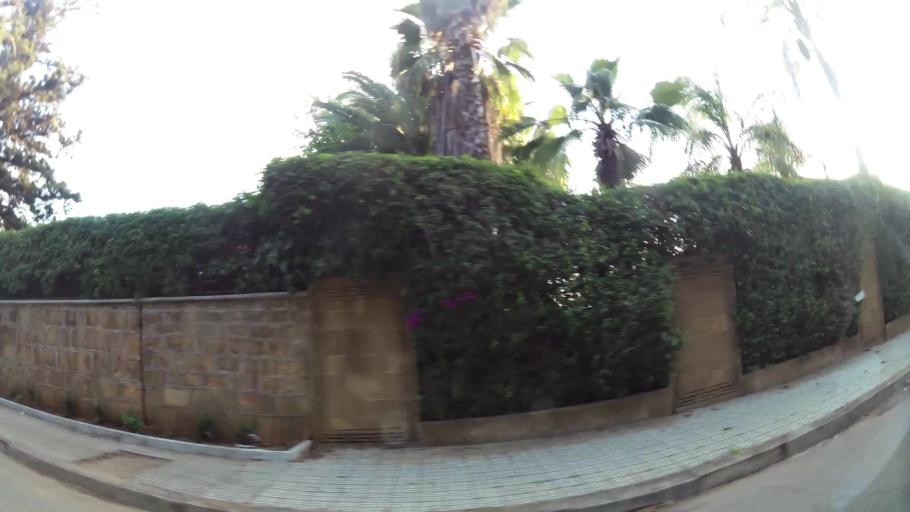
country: MA
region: Rabat-Sale-Zemmour-Zaer
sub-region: Rabat
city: Rabat
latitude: 33.9780
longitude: -6.8328
